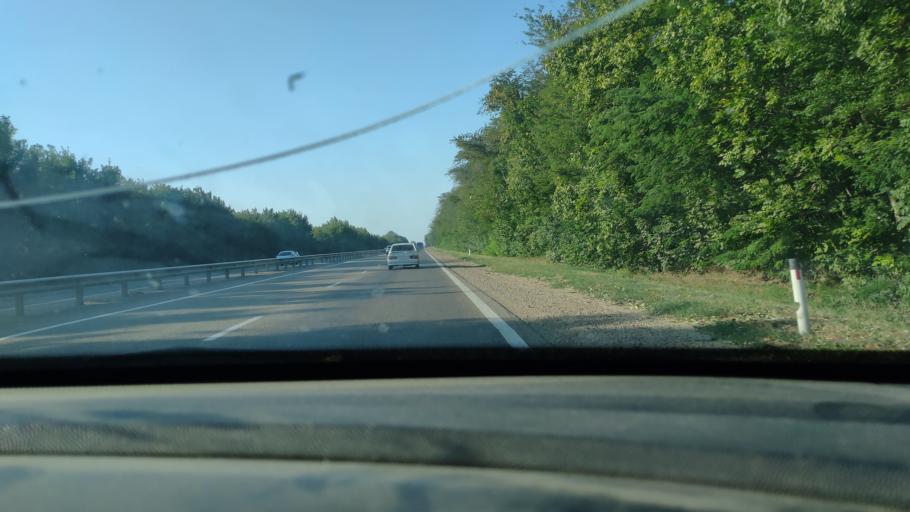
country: RU
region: Krasnodarskiy
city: Timashevsk
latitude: 45.5300
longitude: 38.9405
